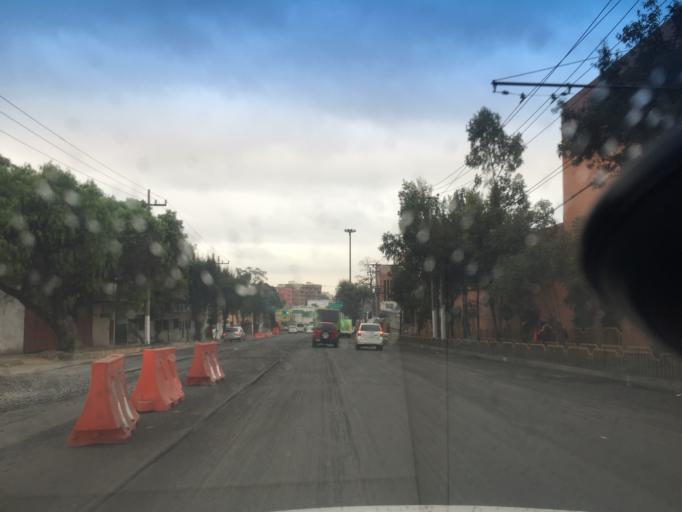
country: MX
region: Mexico City
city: Gustavo A. Madero
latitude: 19.4884
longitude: -99.1158
